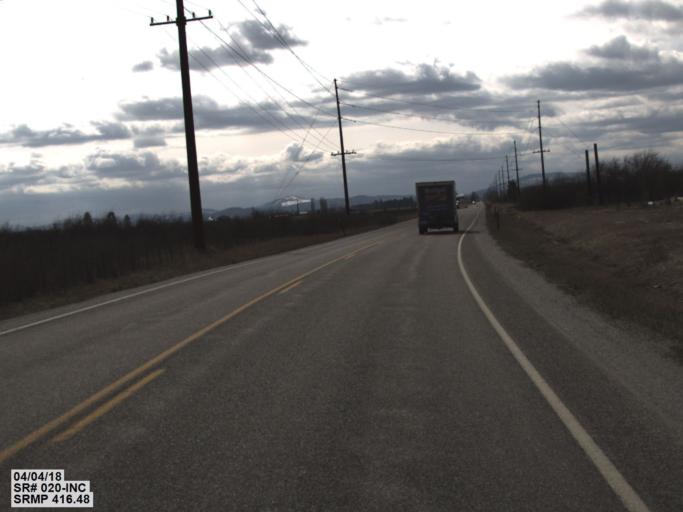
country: US
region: Washington
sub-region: Pend Oreille County
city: Newport
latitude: 48.3743
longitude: -117.3048
